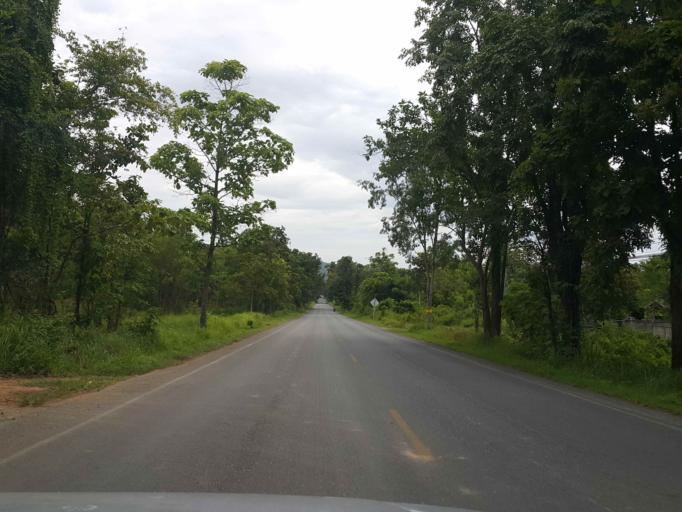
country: TH
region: Lampang
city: Thoen
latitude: 17.5803
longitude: 99.3293
